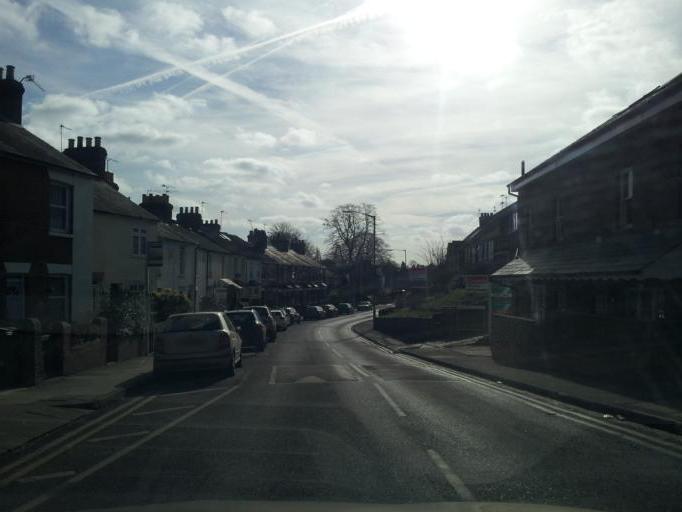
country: GB
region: England
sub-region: Hertfordshire
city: St Albans
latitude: 51.7511
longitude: -0.3233
